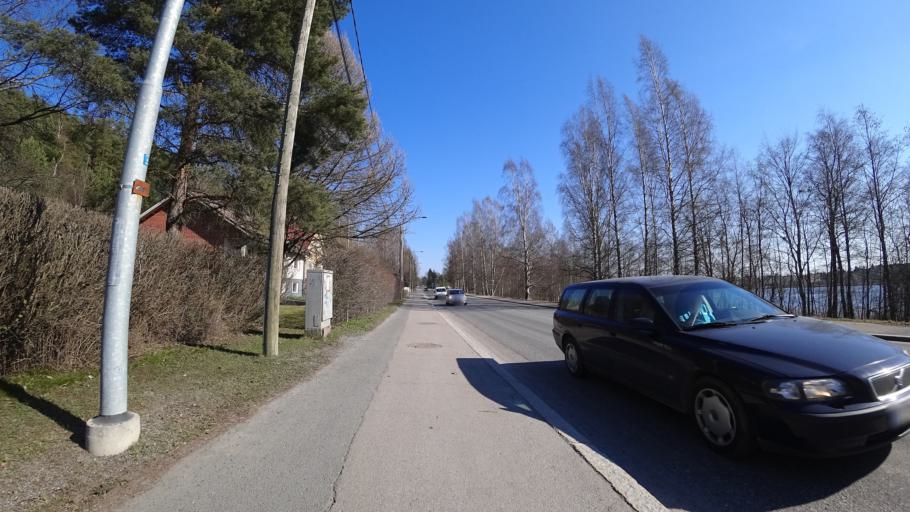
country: FI
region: Pirkanmaa
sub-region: Tampere
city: Pirkkala
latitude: 61.5128
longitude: 23.6568
